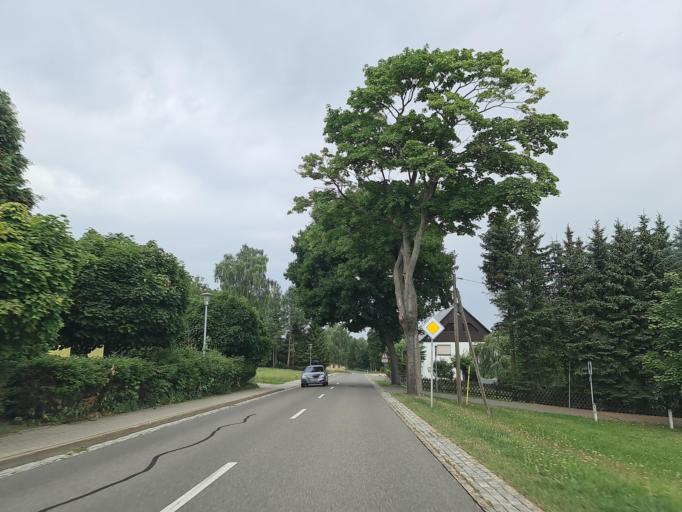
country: DE
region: Saxony
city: Grosshartmannsdorf
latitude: 50.7688
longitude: 13.3359
